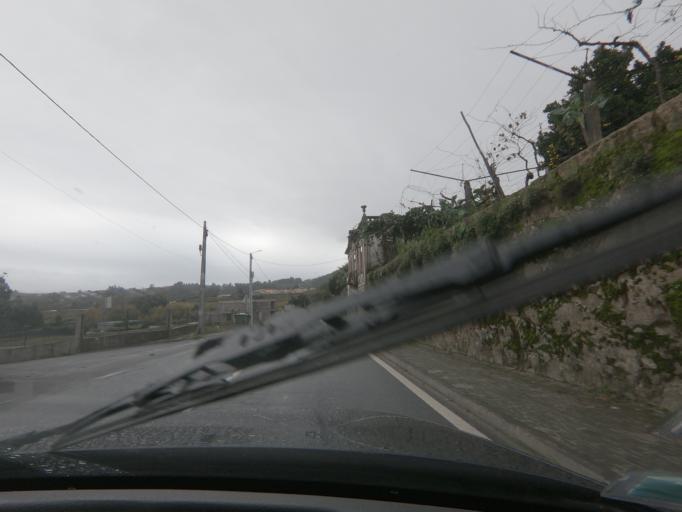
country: PT
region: Braga
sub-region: Celorico de Basto
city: Celorico de Basto
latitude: 41.4198
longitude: -7.9895
